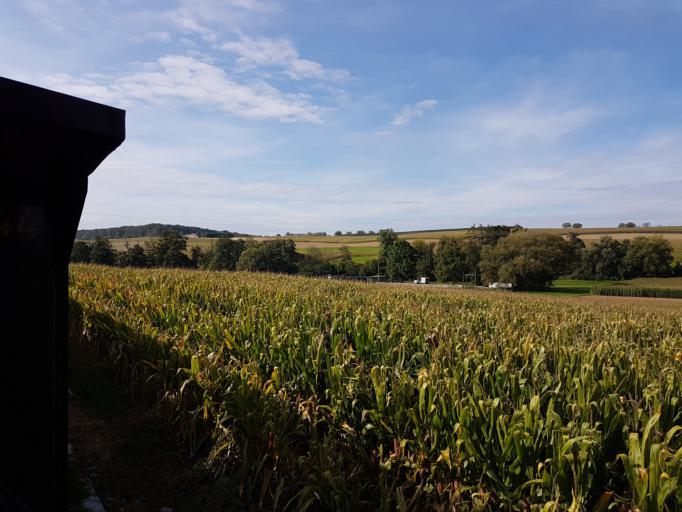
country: DE
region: Baden-Wuerttemberg
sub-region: Freiburg Region
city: Wittlingen
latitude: 47.6798
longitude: 7.6444
